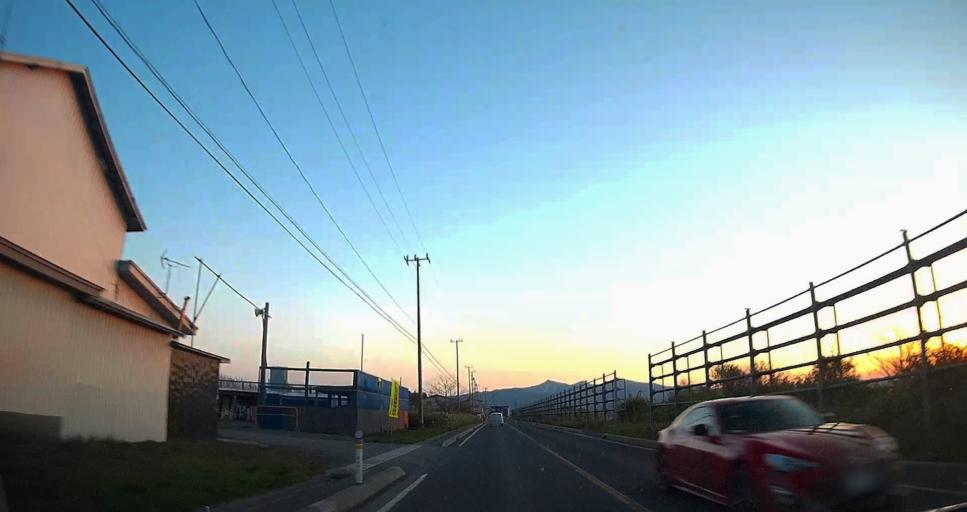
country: JP
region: Aomori
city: Misawa
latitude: 40.8784
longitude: 141.1478
